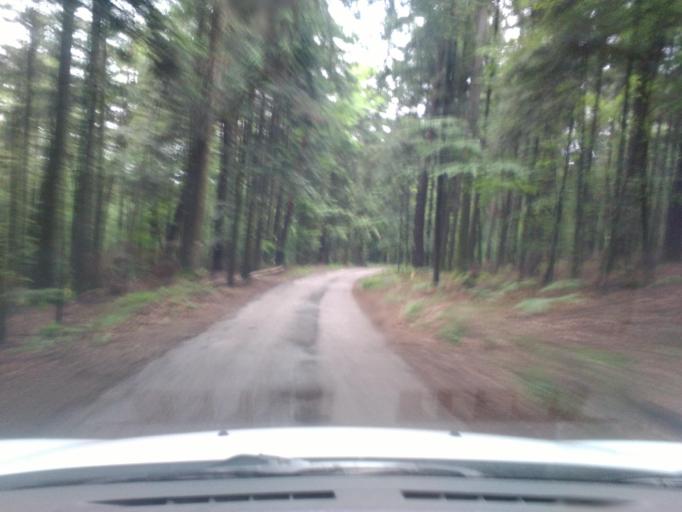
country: FR
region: Lorraine
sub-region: Departement des Vosges
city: Le Tholy
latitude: 48.1216
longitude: 6.6885
